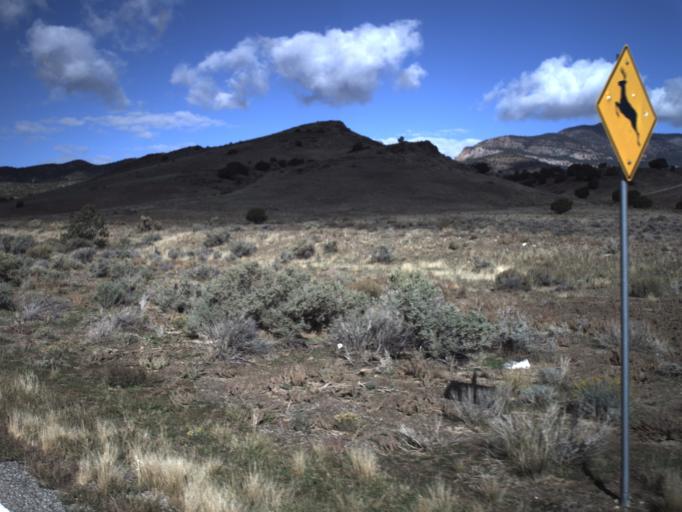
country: US
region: Utah
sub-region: Beaver County
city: Milford
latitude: 38.4613
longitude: -113.2390
